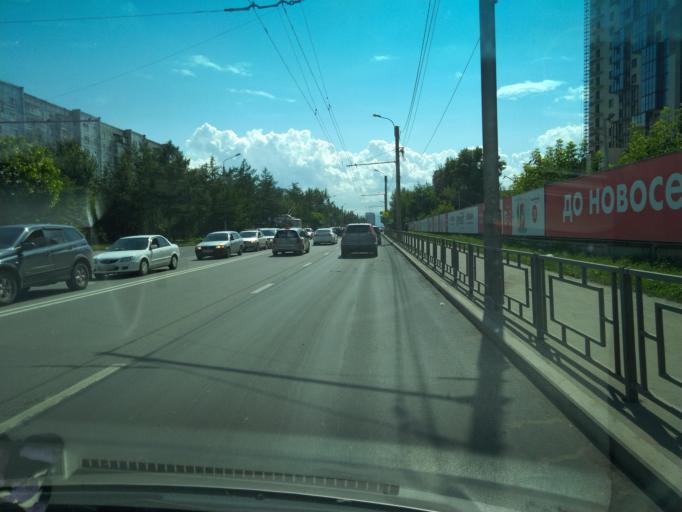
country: RU
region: Krasnoyarskiy
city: Solnechnyy
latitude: 56.0536
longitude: 92.9412
